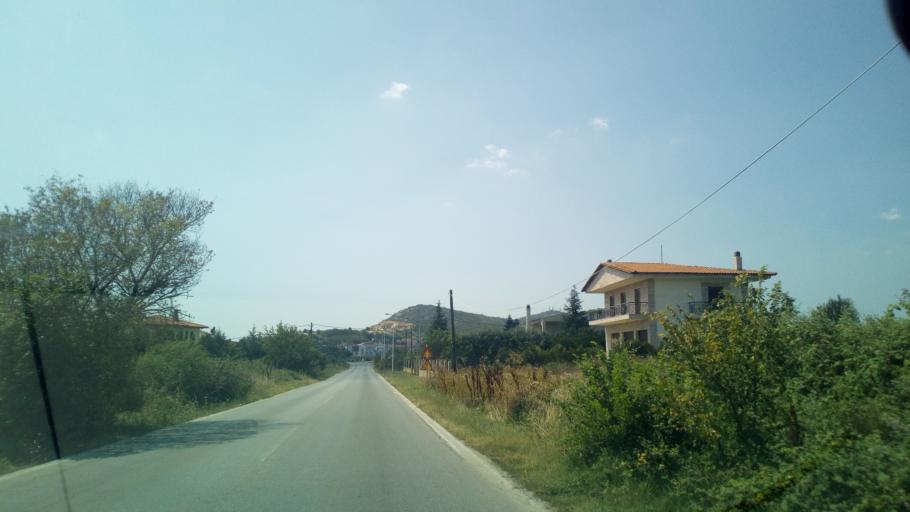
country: GR
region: Central Macedonia
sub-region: Nomos Thessalonikis
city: Chortiatis
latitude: 40.6289
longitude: 23.0959
